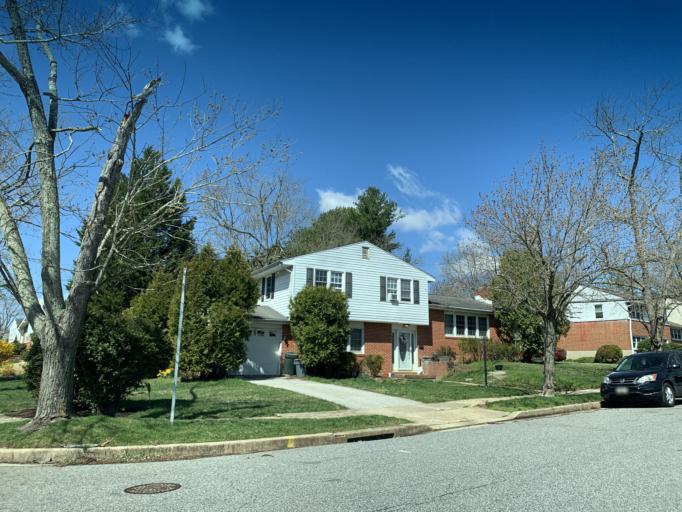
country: US
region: Maryland
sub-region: Baltimore County
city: Timonium
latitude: 39.4417
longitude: -76.6109
